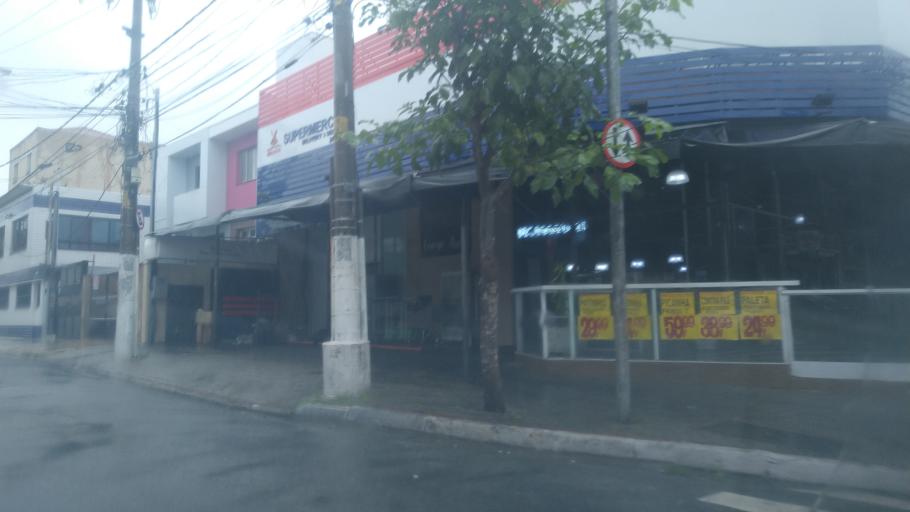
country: BR
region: Sao Paulo
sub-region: Sao Paulo
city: Sao Paulo
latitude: -23.4967
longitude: -46.6153
